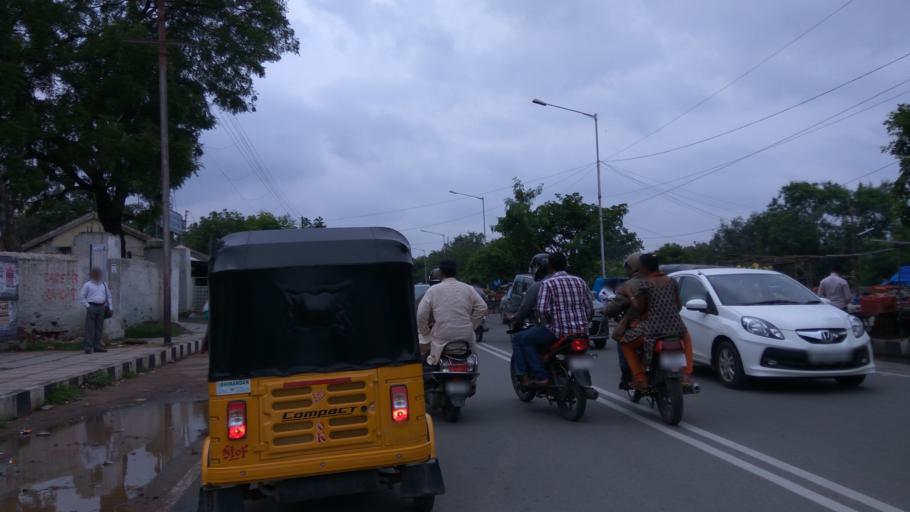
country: IN
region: Telangana
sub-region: Hyderabad
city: Malkajgiri
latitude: 17.4394
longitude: 78.5263
